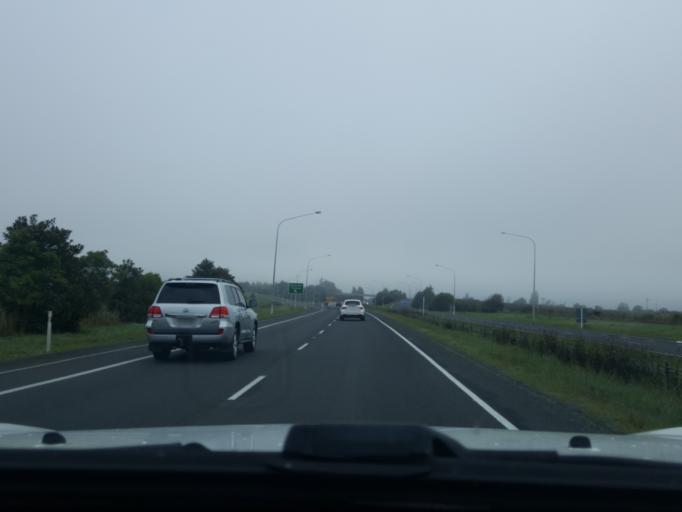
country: NZ
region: Waikato
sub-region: Waikato District
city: Te Kauwhata
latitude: -37.4944
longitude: 175.1623
